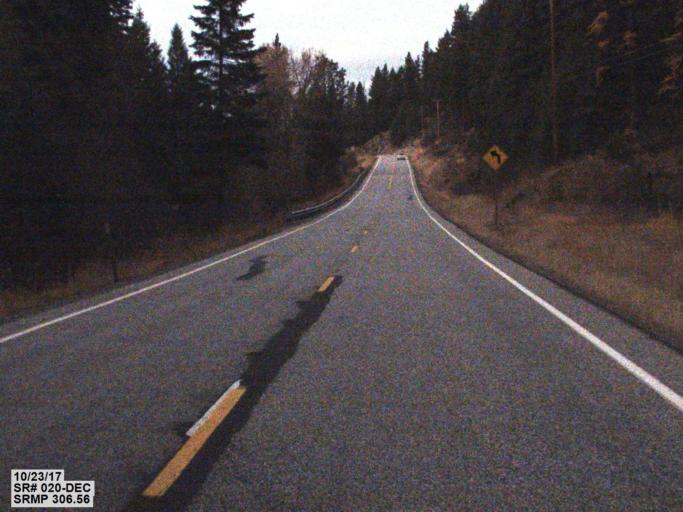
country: US
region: Washington
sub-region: Ferry County
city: Republic
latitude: 48.6336
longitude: -118.6771
